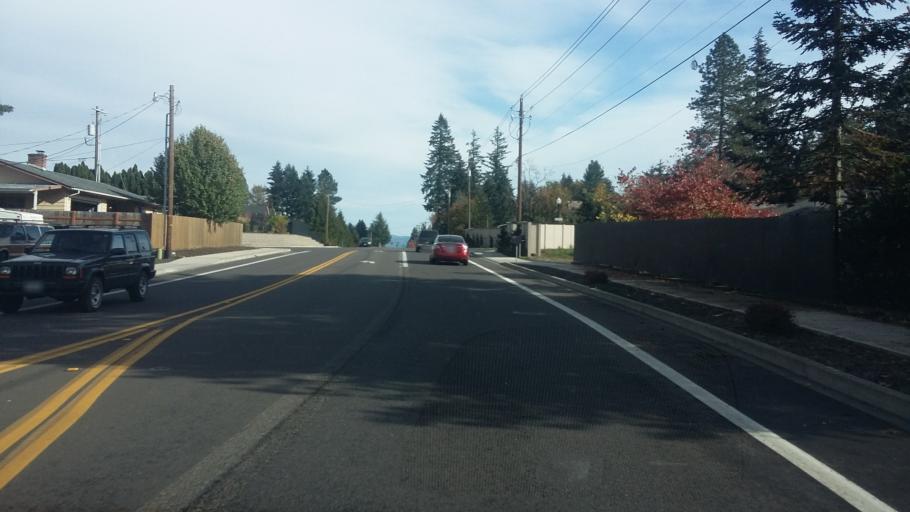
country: US
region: Washington
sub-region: Clark County
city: Salmon Creek
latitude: 45.6859
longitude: -122.6318
